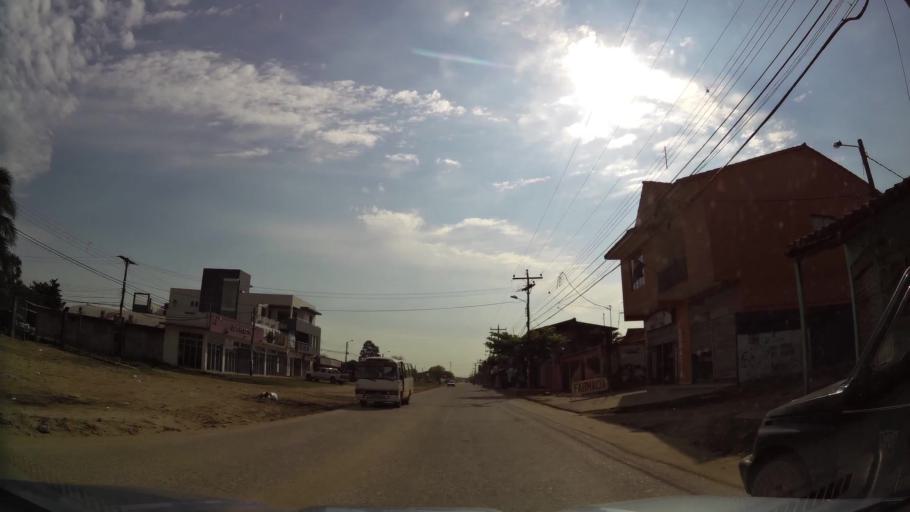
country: BO
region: Santa Cruz
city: Santa Cruz de la Sierra
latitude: -17.7326
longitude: -63.1423
